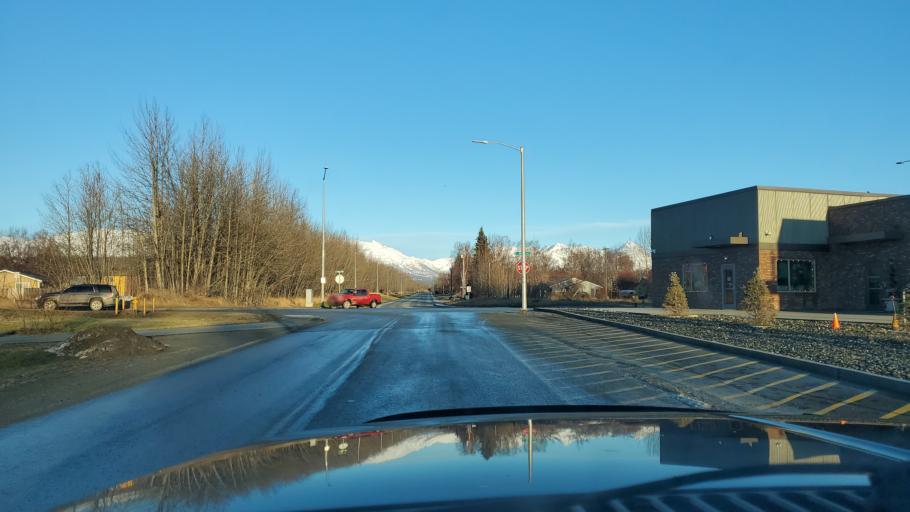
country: US
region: Alaska
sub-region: Matanuska-Susitna Borough
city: Palmer
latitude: 61.6062
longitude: -149.1103
